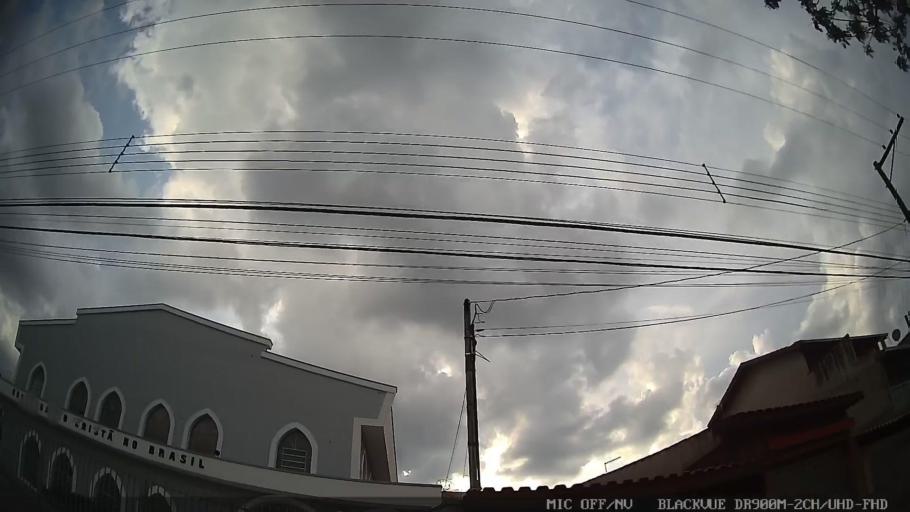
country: BR
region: Sao Paulo
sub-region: Braganca Paulista
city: Braganca Paulista
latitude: -22.9149
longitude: -46.5271
